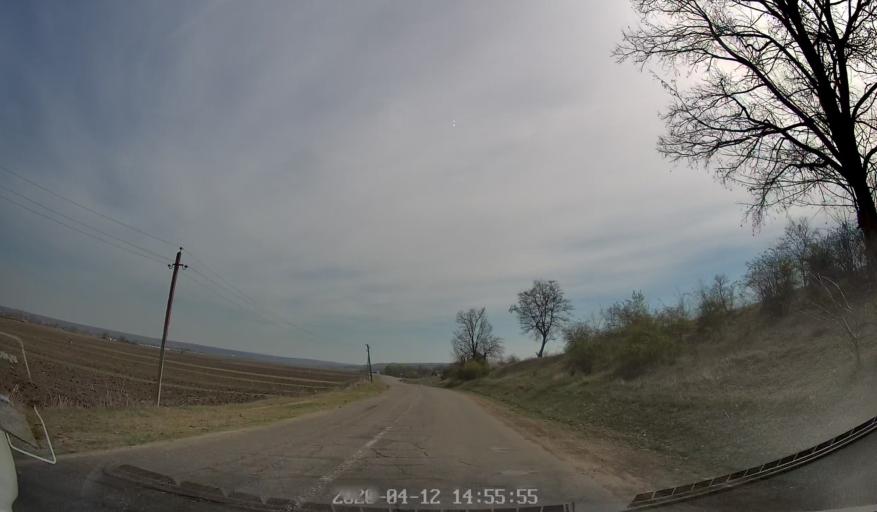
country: MD
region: Telenesti
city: Dubasari
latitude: 47.2663
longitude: 29.1259
